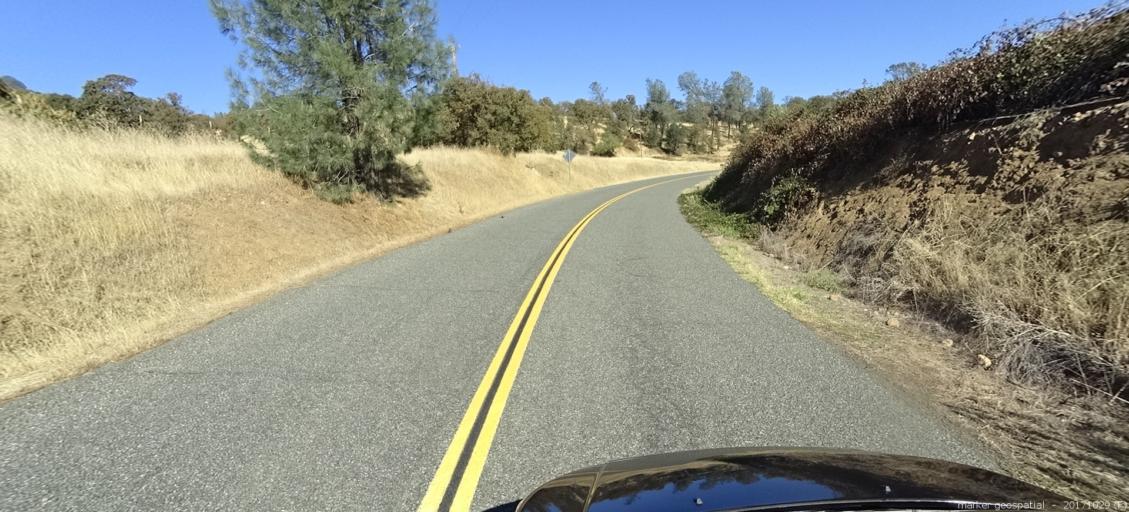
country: US
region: California
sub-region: Shasta County
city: Shasta
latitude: 40.4563
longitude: -122.6332
